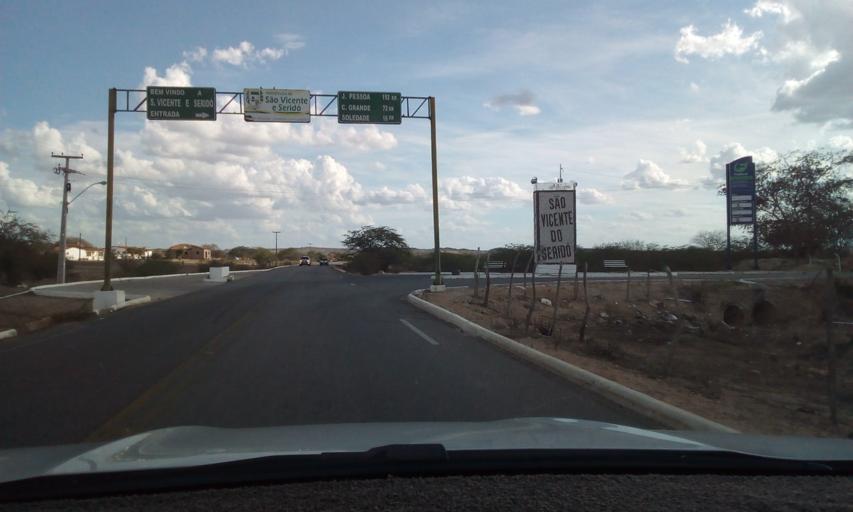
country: BR
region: Paraiba
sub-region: Soledade
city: Soledade
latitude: -6.9375
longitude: -36.3858
